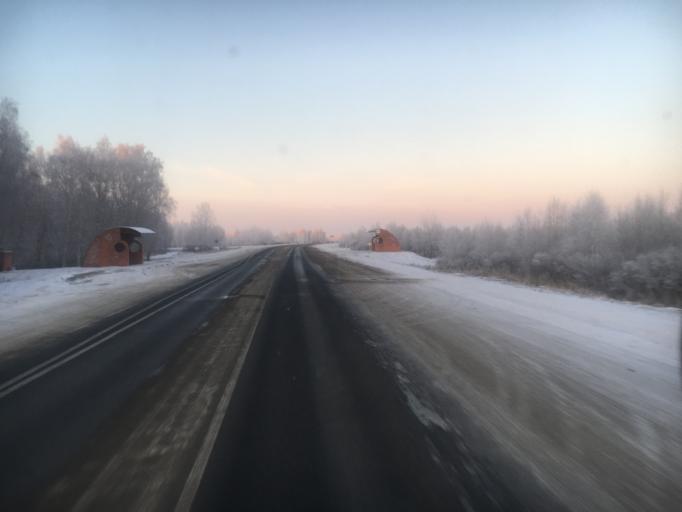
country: KZ
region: Soltustik Qazaqstan
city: Smirnovo
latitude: 54.4773
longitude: 69.2214
